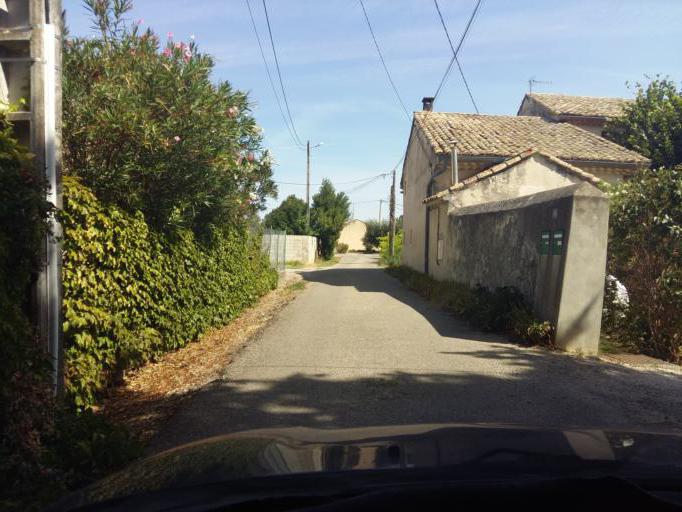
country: FR
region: Provence-Alpes-Cote d'Azur
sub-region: Departement du Vaucluse
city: Camaret-sur-Aigues
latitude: 44.1706
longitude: 4.8762
